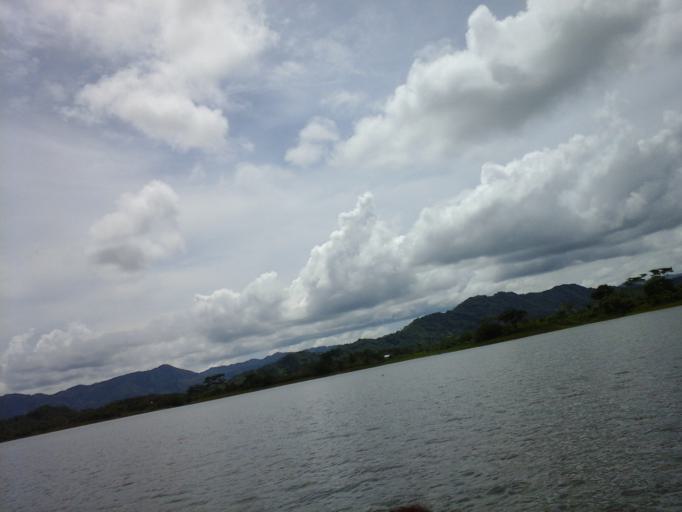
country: CO
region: Bolivar
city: San Cristobal
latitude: 9.8729
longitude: -75.2979
